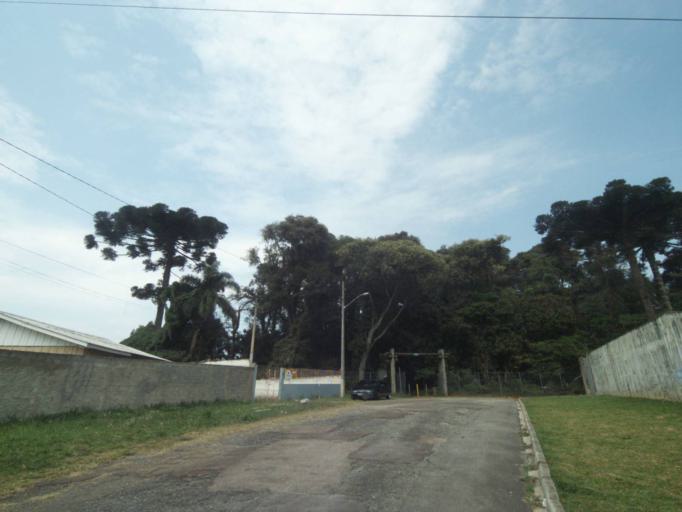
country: BR
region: Parana
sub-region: Curitiba
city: Curitiba
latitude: -25.4747
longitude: -49.3206
